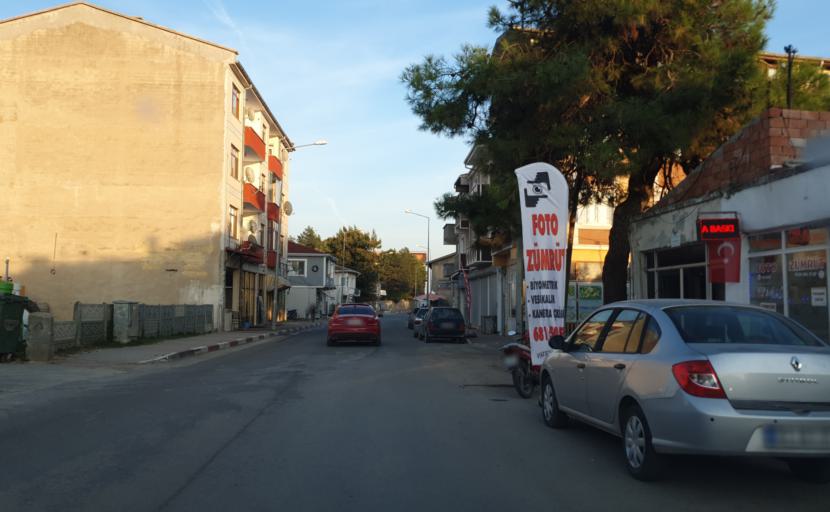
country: TR
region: Kirklareli
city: Sergen
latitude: 41.8249
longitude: 27.7685
